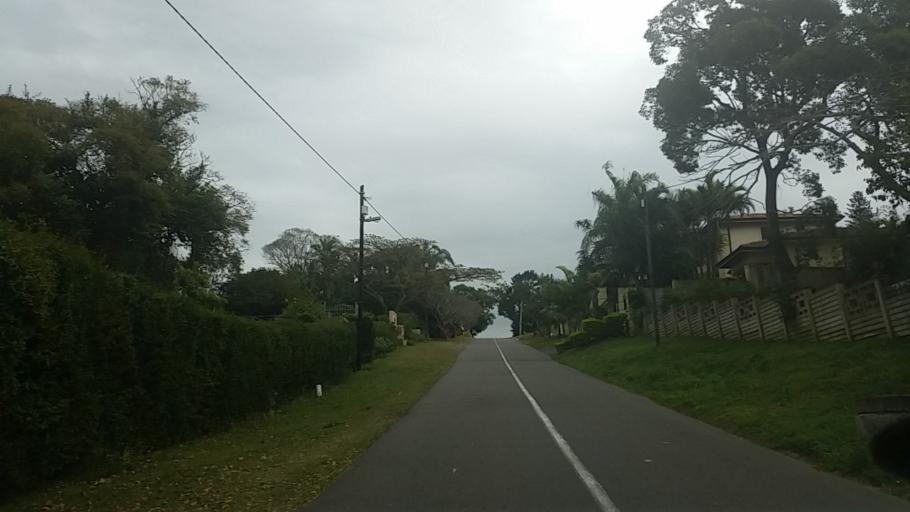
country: ZA
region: KwaZulu-Natal
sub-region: eThekwini Metropolitan Municipality
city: Berea
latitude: -29.8447
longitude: 30.9303
